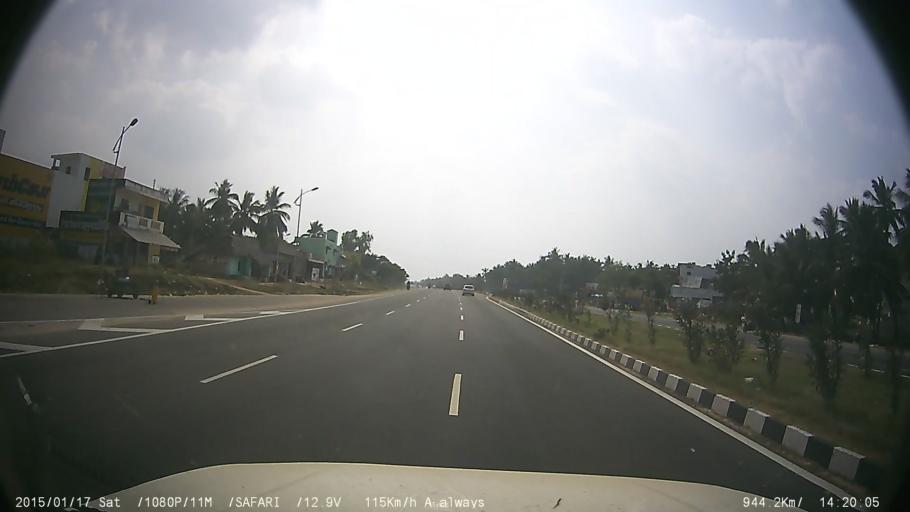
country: IN
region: Tamil Nadu
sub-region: Vellore
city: Vaniyambadi
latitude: 12.7131
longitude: 78.6553
